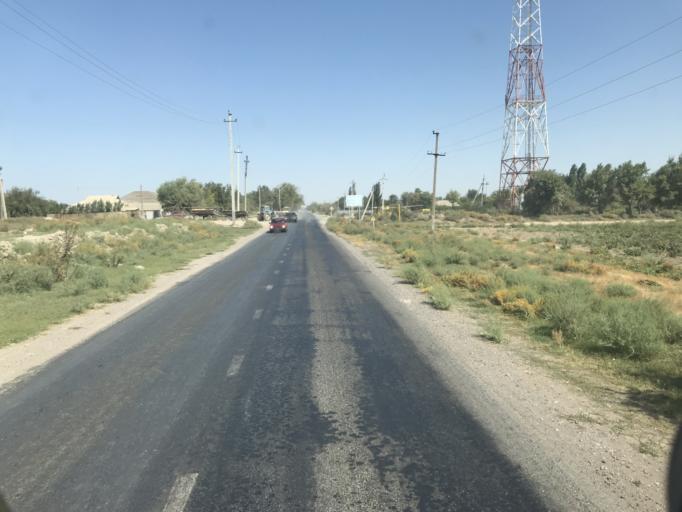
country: KZ
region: Ongtustik Qazaqstan
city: Ilyich
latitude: 40.9265
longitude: 68.4883
